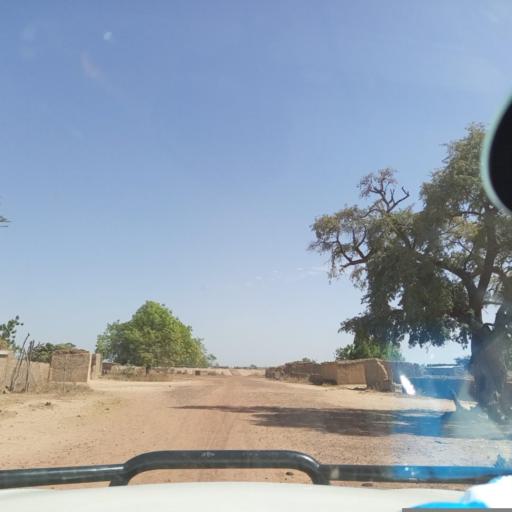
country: ML
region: Koulikoro
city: Dioila
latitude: 12.5211
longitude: -6.8089
